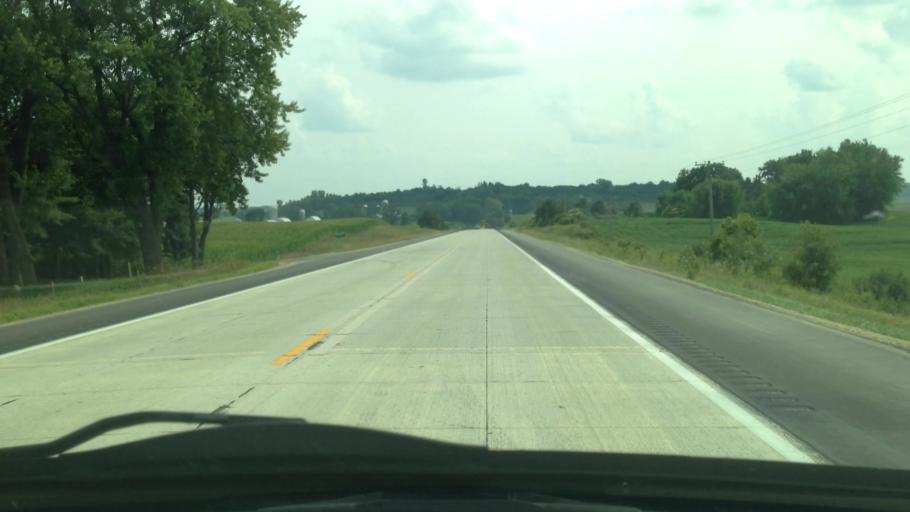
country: US
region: Minnesota
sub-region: Olmsted County
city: Oronoco
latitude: 44.1549
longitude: -92.4194
